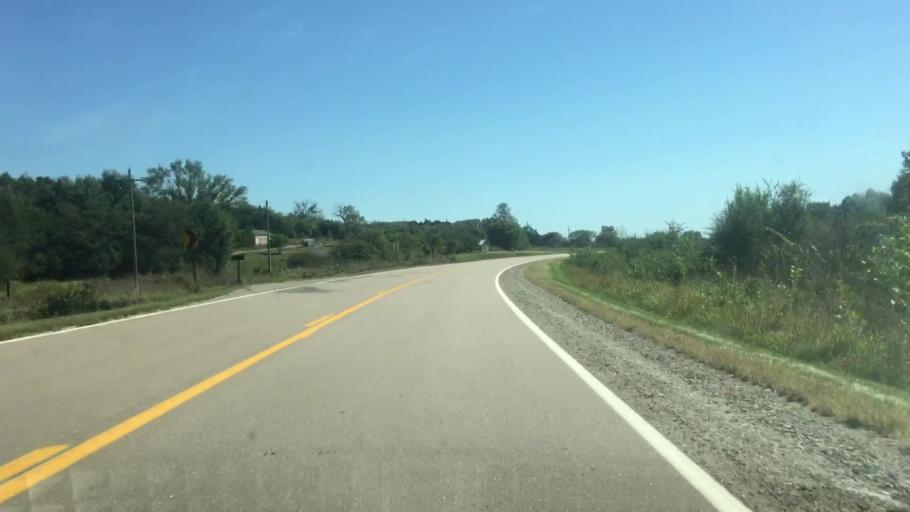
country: US
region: Nebraska
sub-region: Jefferson County
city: Fairbury
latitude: 40.0738
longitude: -97.0710
